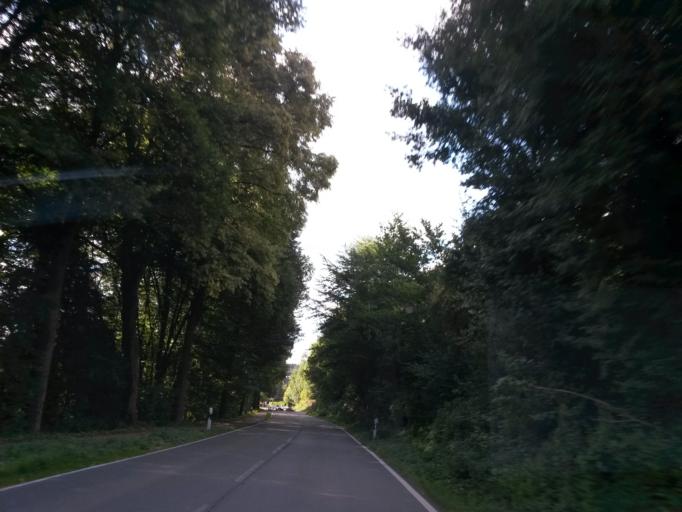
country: DE
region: North Rhine-Westphalia
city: Waldbrol
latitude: 50.8971
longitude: 7.6285
